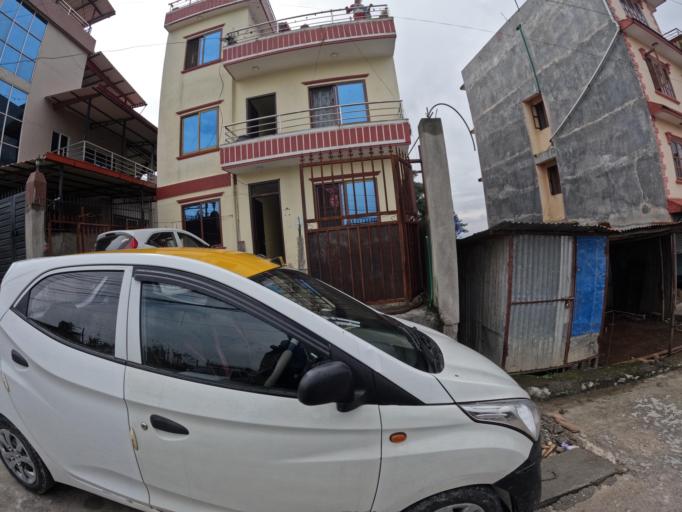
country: NP
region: Central Region
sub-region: Bagmati Zone
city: Kathmandu
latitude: 27.7589
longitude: 85.3229
